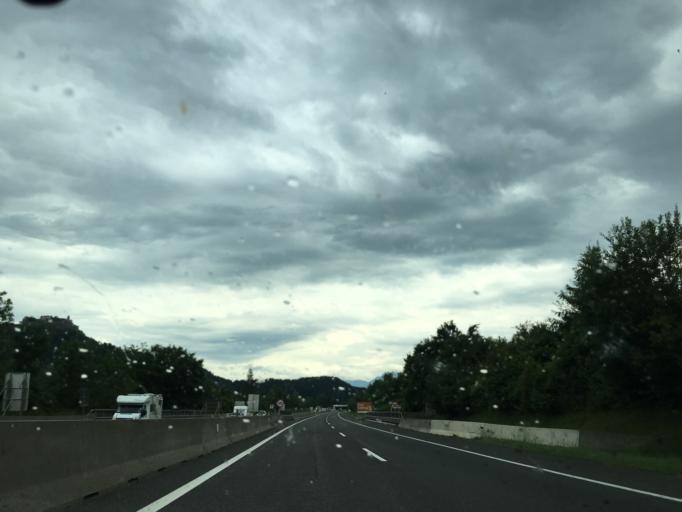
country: AT
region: Carinthia
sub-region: Villach Stadt
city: Villach
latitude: 46.6468
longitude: 13.8799
